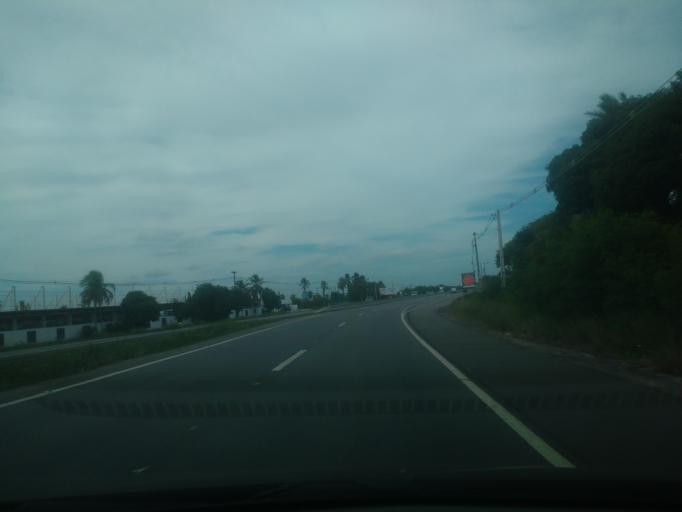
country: BR
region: Alagoas
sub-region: Maceio
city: Maceio
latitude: -9.7029
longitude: -35.8049
